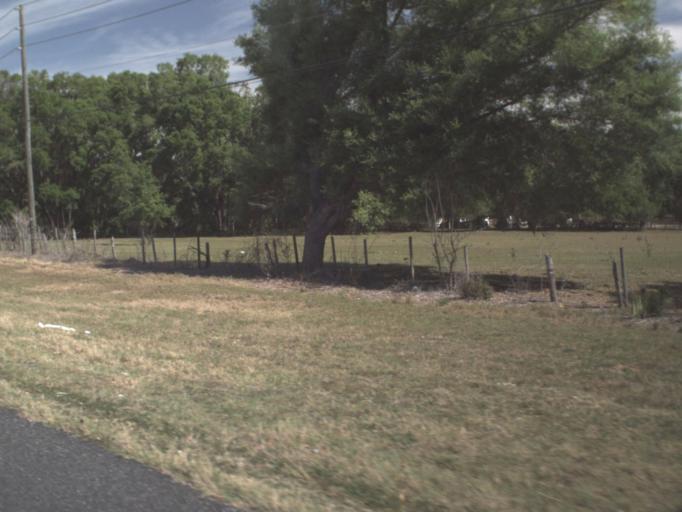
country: US
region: Florida
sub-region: Marion County
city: Belleview
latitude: 29.0246
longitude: -82.0184
